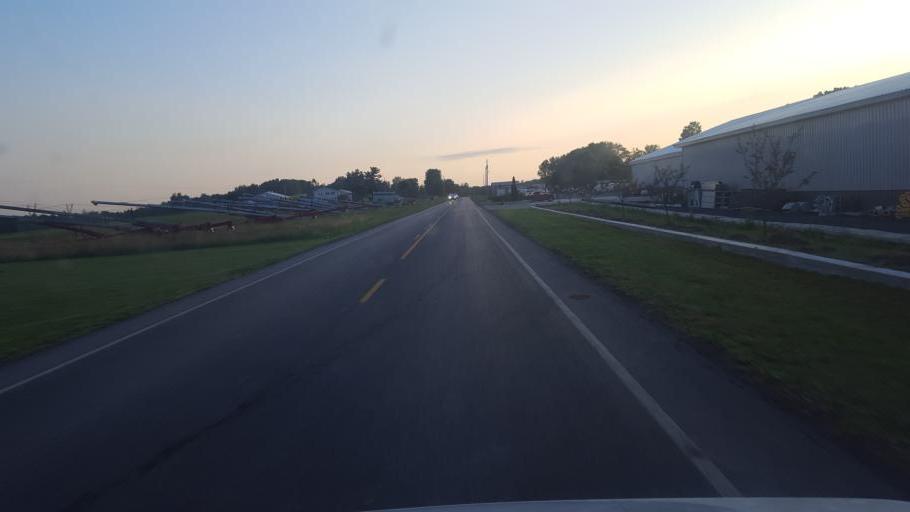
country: US
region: New York
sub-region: Wayne County
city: Clyde
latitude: 43.0506
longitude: -76.9001
